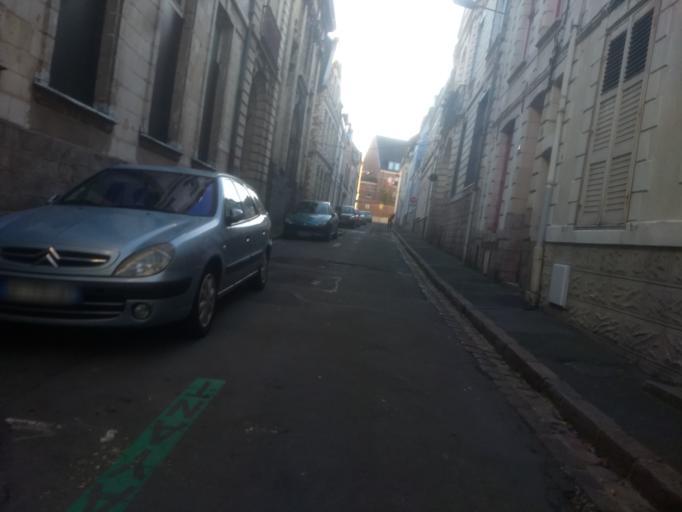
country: FR
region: Nord-Pas-de-Calais
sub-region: Departement du Pas-de-Calais
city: Arras
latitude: 50.2934
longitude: 2.7754
